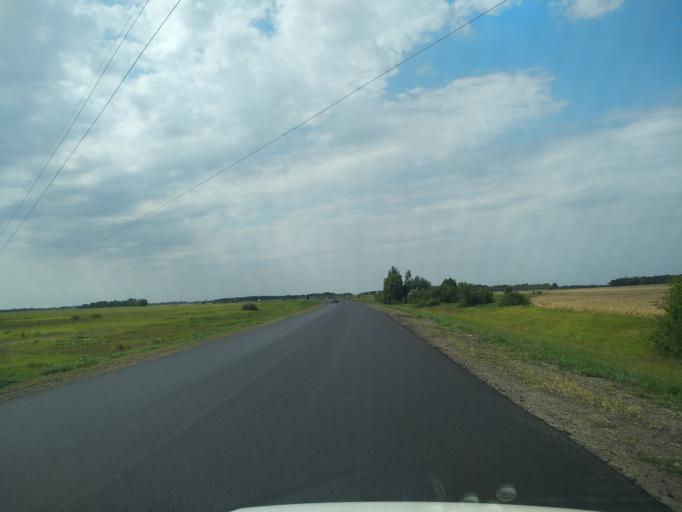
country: RU
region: Voronezj
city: Pereleshino
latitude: 51.7821
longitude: 40.1390
